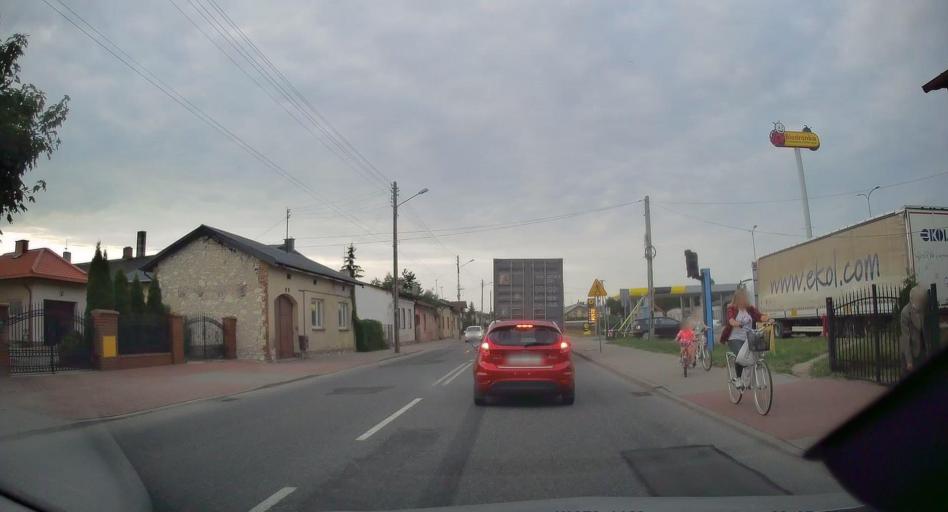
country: PL
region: Lodz Voivodeship
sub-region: Powiat radomszczanski
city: Kamiensk
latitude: 51.1945
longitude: 19.4987
